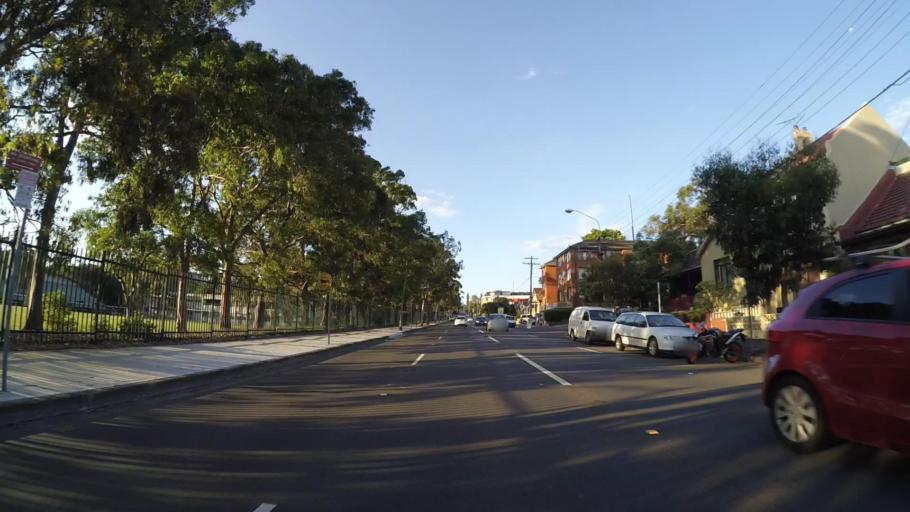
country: AU
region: New South Wales
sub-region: Randwick
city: Daceyville
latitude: -33.9232
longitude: 151.2399
